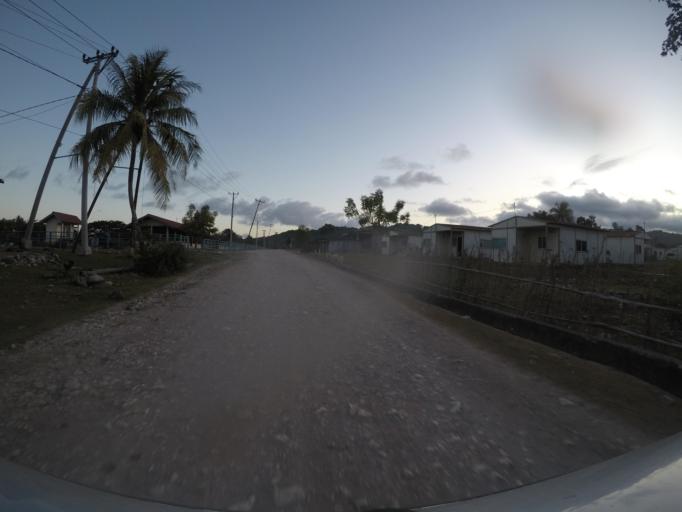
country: TL
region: Viqueque
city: Viqueque
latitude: -8.7735
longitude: 126.6388
